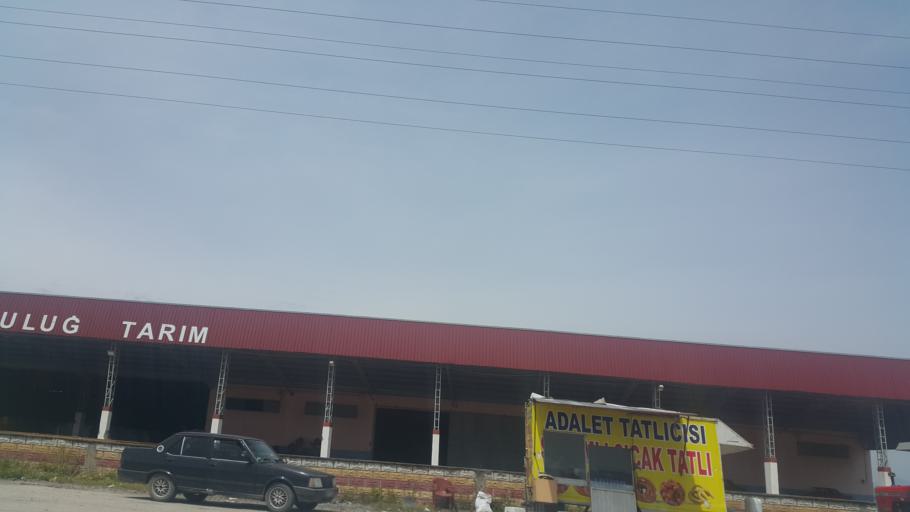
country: TR
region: Adana
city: Kosreli
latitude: 37.0688
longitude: 36.0000
